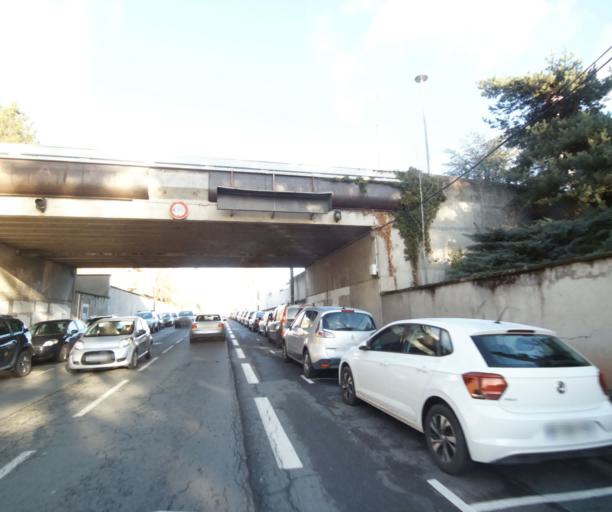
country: FR
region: Rhone-Alpes
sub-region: Departement de la Loire
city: Le Coteau
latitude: 46.0431
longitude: 4.0811
